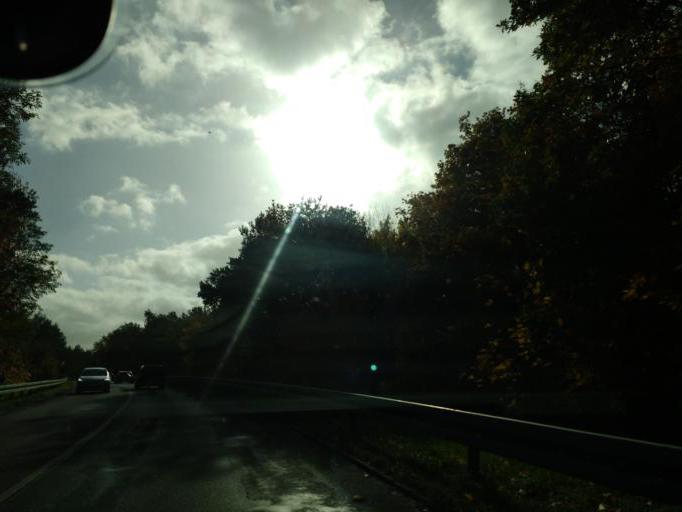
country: DE
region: Brandenburg
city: Petershagen
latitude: 52.5325
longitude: 13.8186
